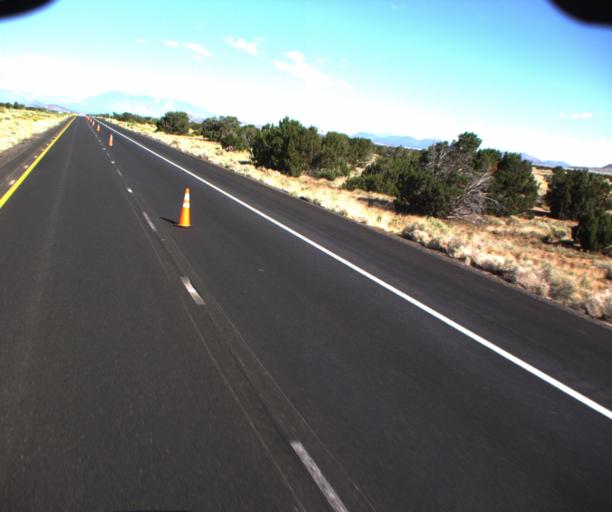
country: US
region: Arizona
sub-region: Coconino County
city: Flagstaff
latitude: 35.1639
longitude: -111.3118
